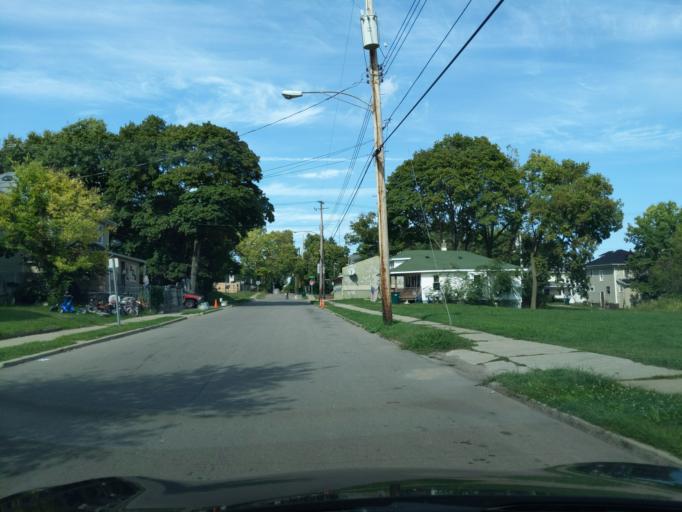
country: US
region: Michigan
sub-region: Ingham County
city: Lansing
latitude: 42.7157
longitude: -84.5419
